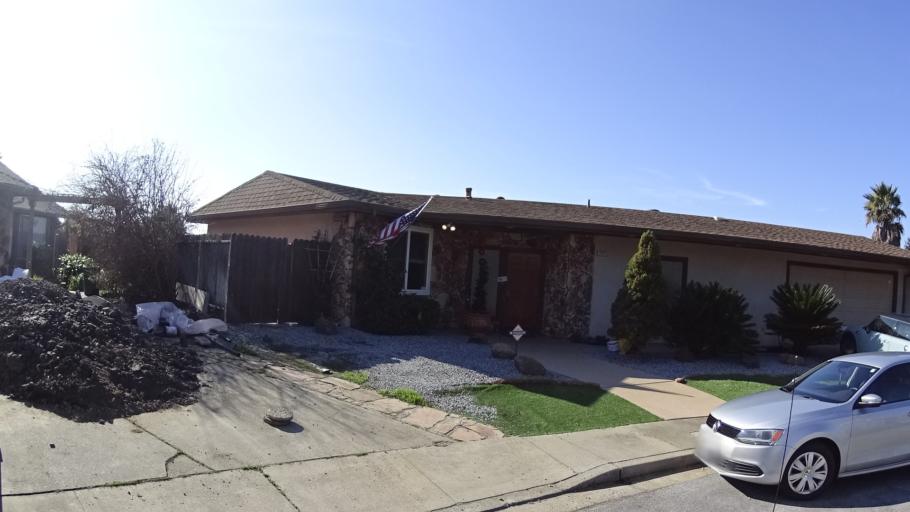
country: US
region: California
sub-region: Alameda County
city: Fairview
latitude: 37.6688
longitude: -122.0497
